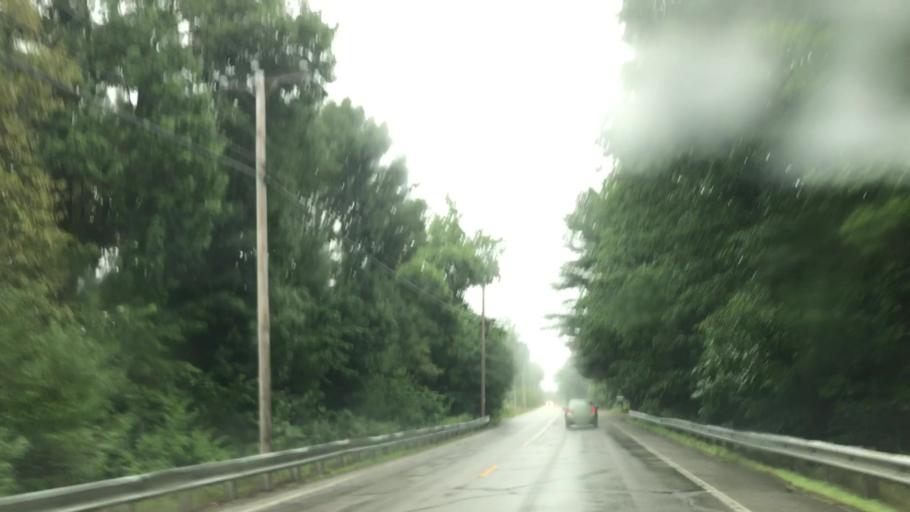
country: US
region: Maine
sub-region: York County
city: Berwick
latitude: 43.2820
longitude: -70.8386
